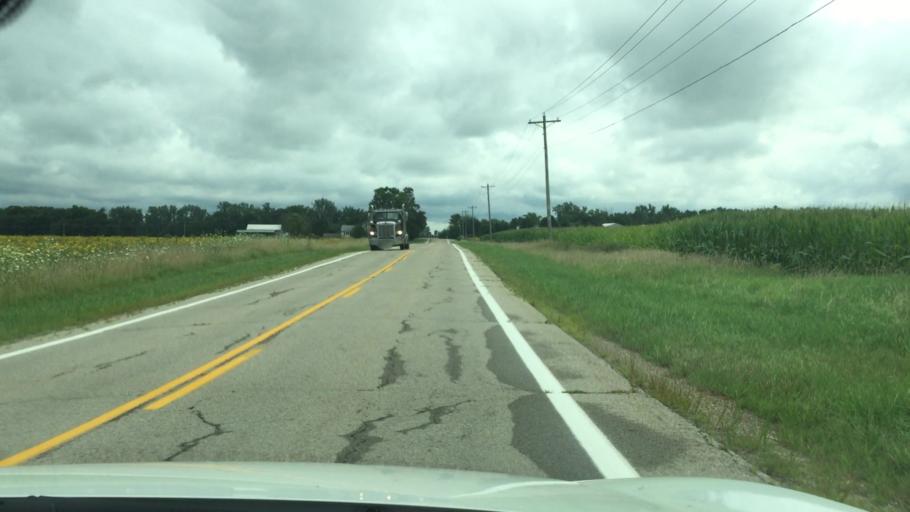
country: US
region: Ohio
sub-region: Champaign County
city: Mechanicsburg
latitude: 40.1264
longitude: -83.5320
